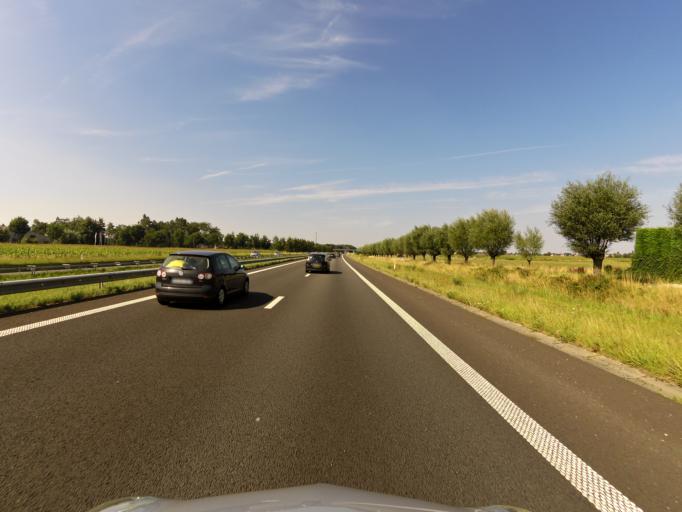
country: BE
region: Flanders
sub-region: Provincie West-Vlaanderen
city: Lichtervelde
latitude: 51.0615
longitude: 3.1572
